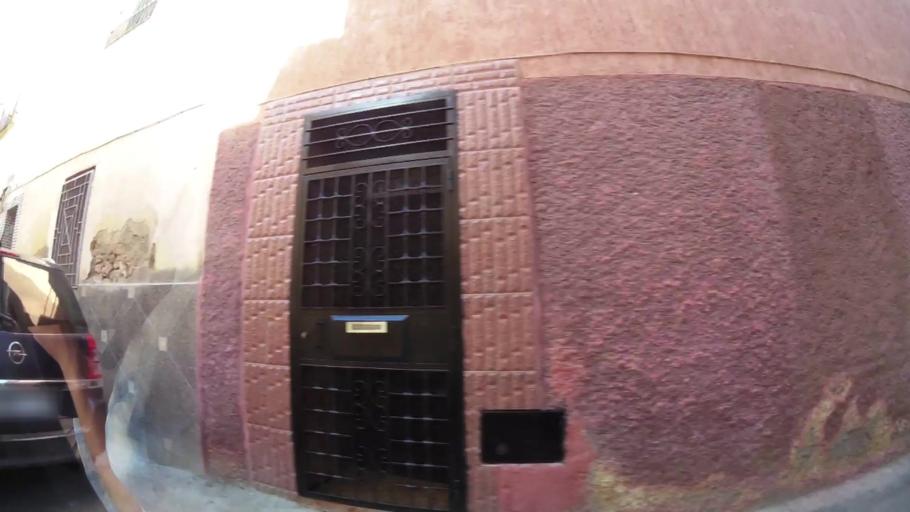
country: MA
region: Oriental
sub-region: Oujda-Angad
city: Oujda
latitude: 34.6946
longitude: -1.9179
